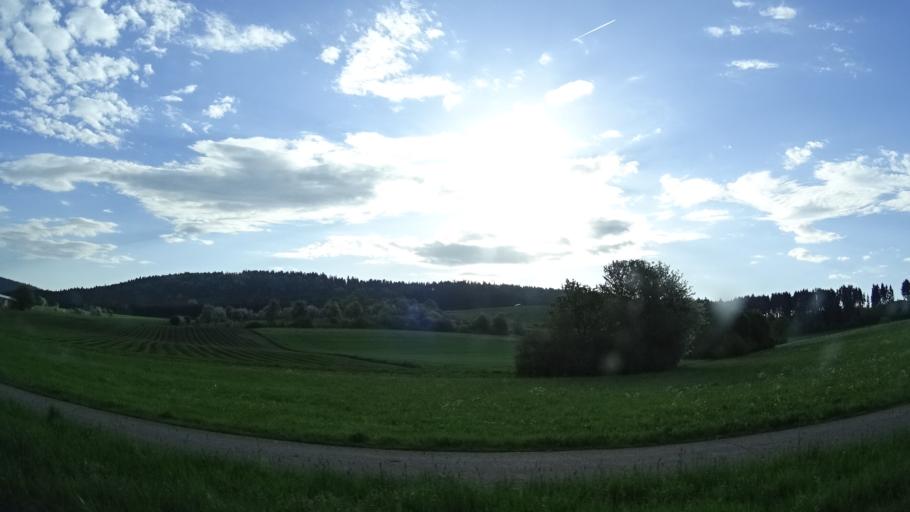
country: DE
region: Baden-Wuerttemberg
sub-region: Freiburg Region
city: Dietingen
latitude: 48.2404
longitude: 8.6629
